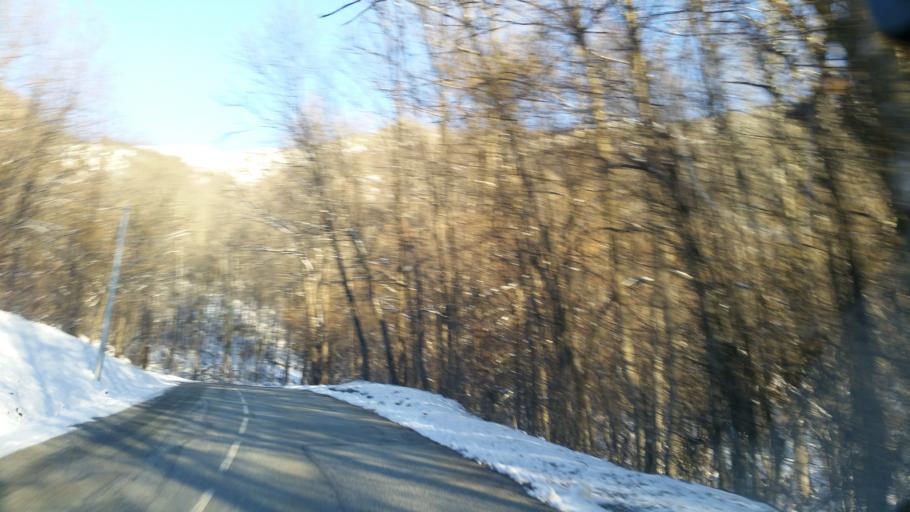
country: FR
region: Rhone-Alpes
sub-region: Departement de la Savoie
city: Saint-Jean-de-Maurienne
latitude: 45.2797
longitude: 6.3239
